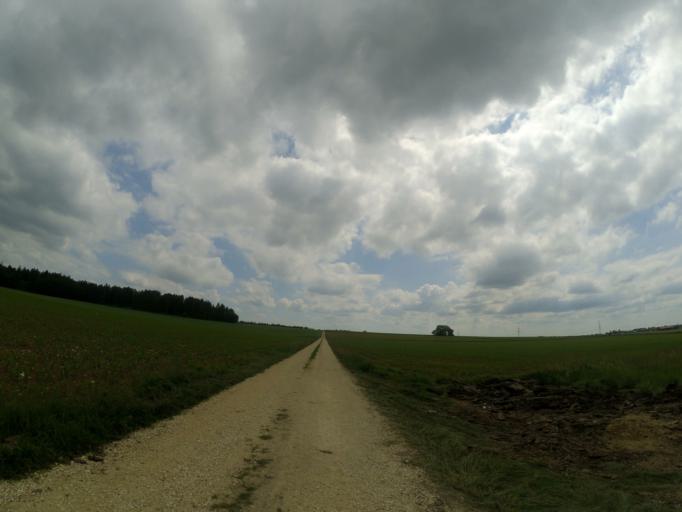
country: DE
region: Baden-Wuerttemberg
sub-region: Tuebingen Region
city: Blaubeuren
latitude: 48.4253
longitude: 9.8295
